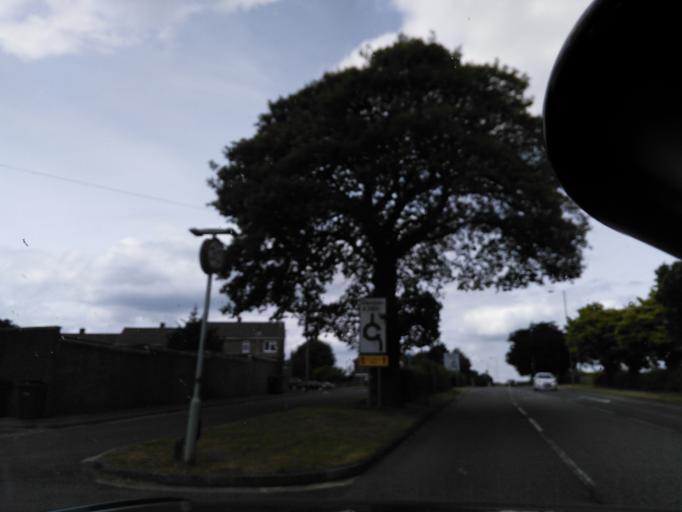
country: GB
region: England
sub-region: Wiltshire
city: Woodford
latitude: 51.0897
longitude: -1.8263
